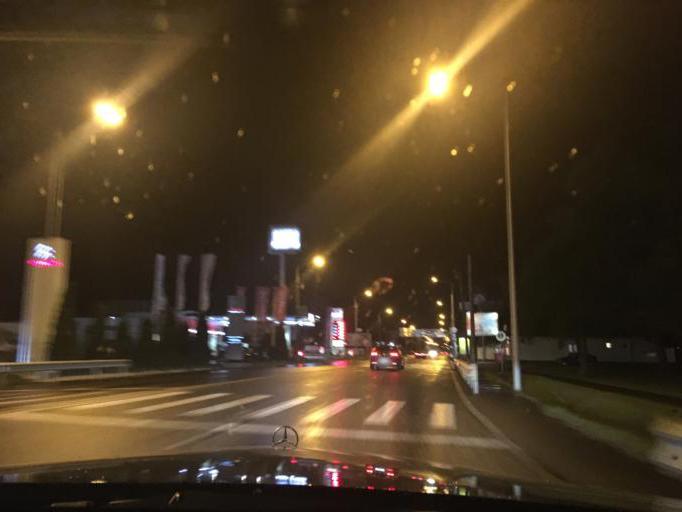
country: RO
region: Bihor
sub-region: Comuna Sanmartin
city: Sanmartin
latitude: 47.0367
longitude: 21.9959
